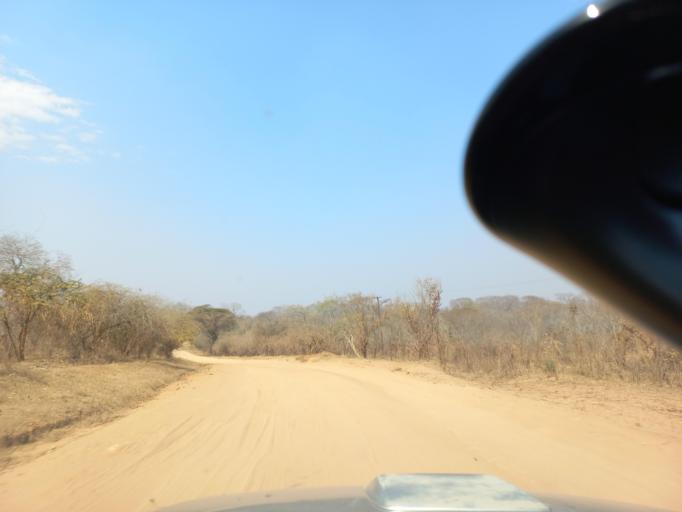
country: ZW
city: Chirundu
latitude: -15.9258
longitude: 28.8853
